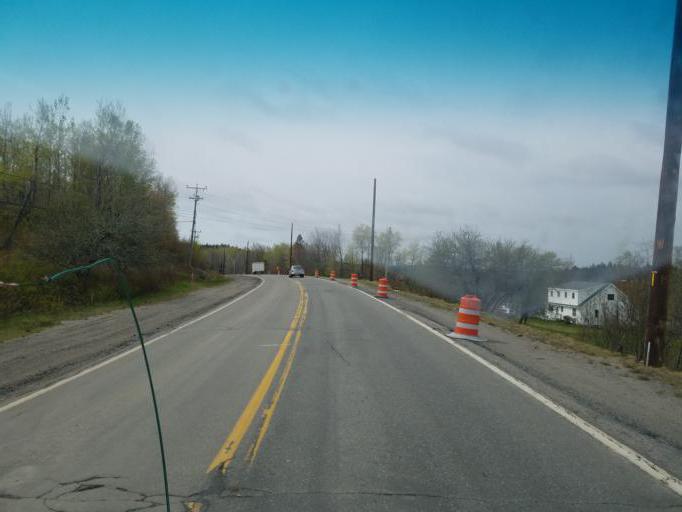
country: US
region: Maine
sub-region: Washington County
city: East Machias
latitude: 44.7808
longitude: -67.1943
